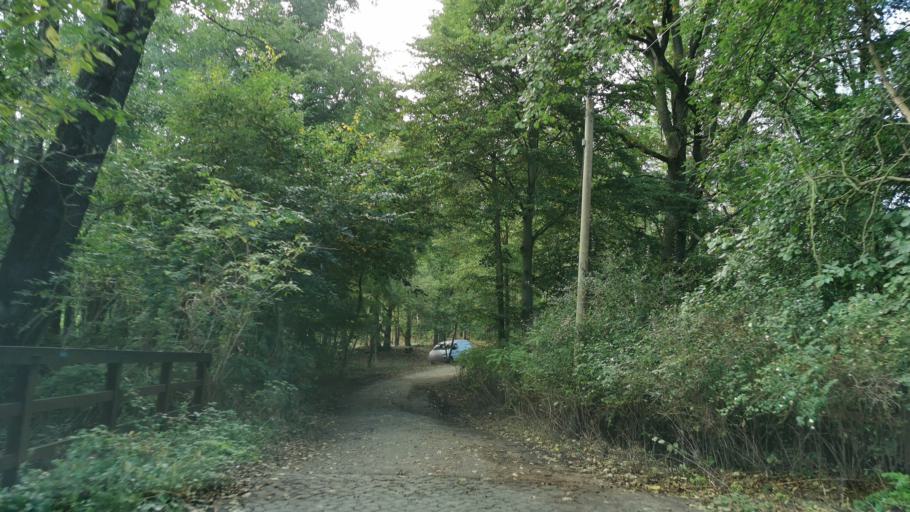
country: DE
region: Brandenburg
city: Michendorf
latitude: 52.3122
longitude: 12.9738
